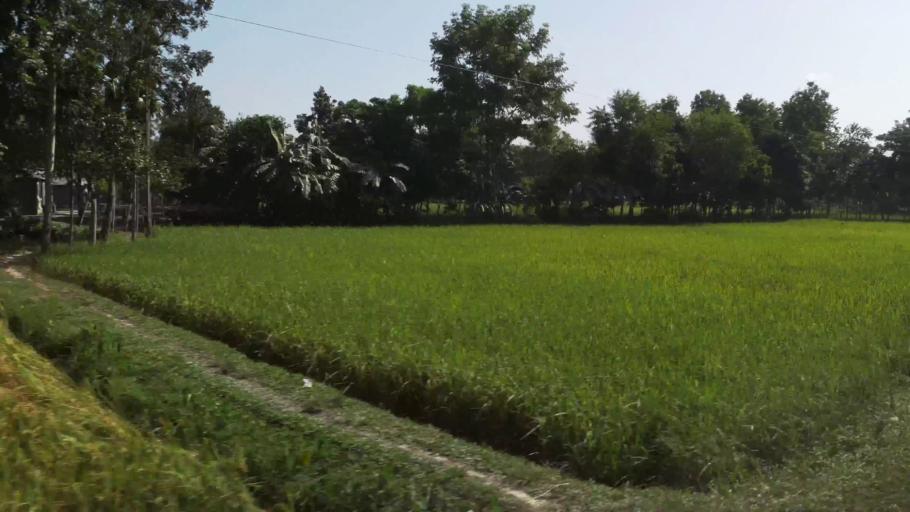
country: BD
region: Dhaka
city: Gafargaon
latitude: 24.5274
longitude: 90.5086
